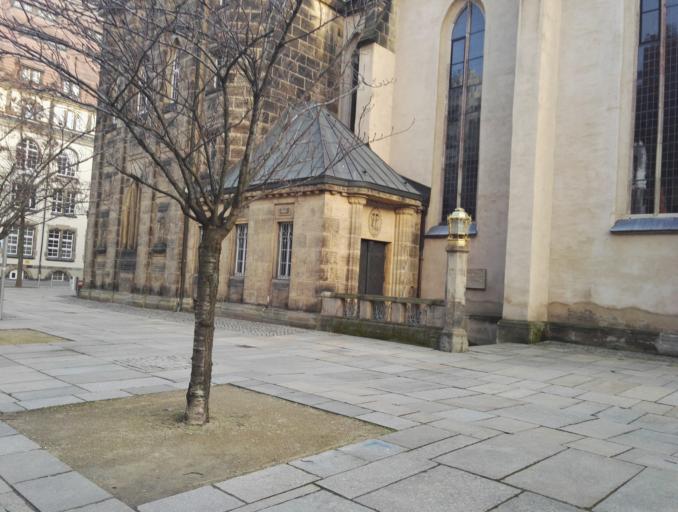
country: DE
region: Saxony
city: Chemnitz
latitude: 50.8332
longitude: 12.9186
